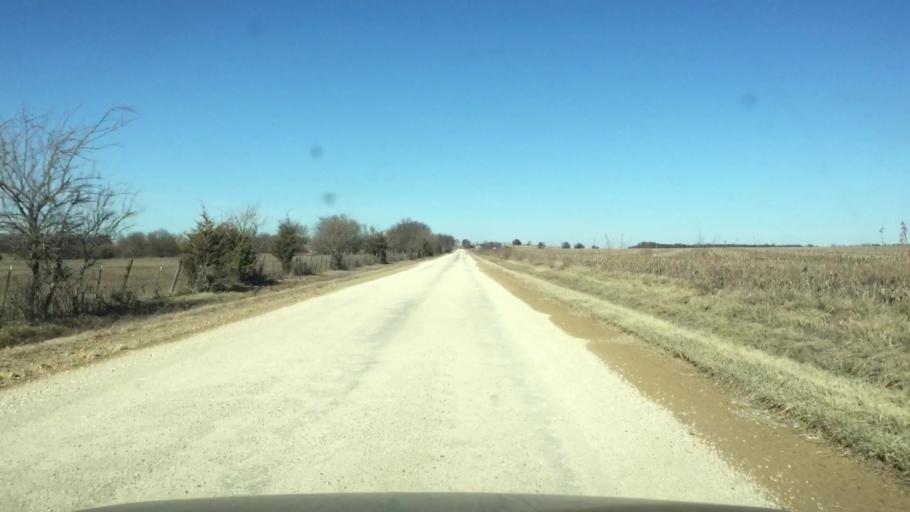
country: US
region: Kansas
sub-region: Allen County
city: Iola
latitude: 37.8651
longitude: -95.3913
